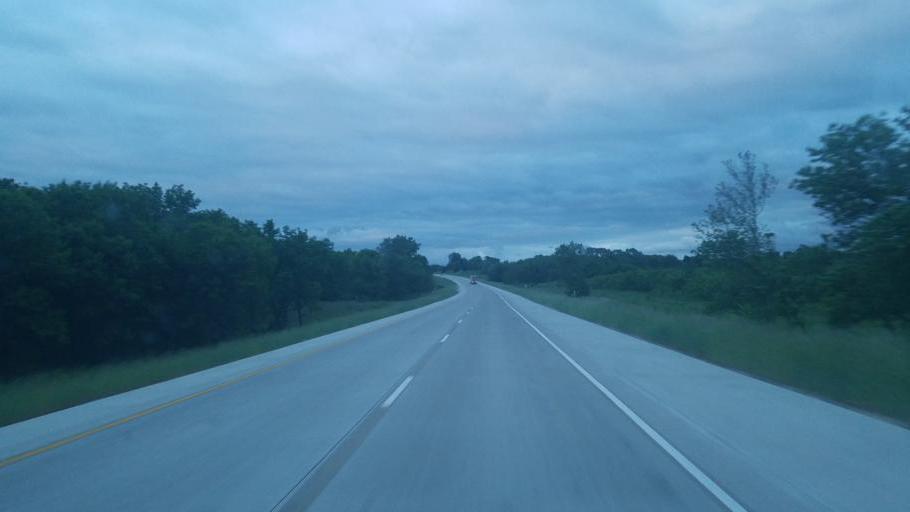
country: US
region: Iowa
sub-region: Decatur County
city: Lamoni
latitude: 40.5960
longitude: -93.9137
